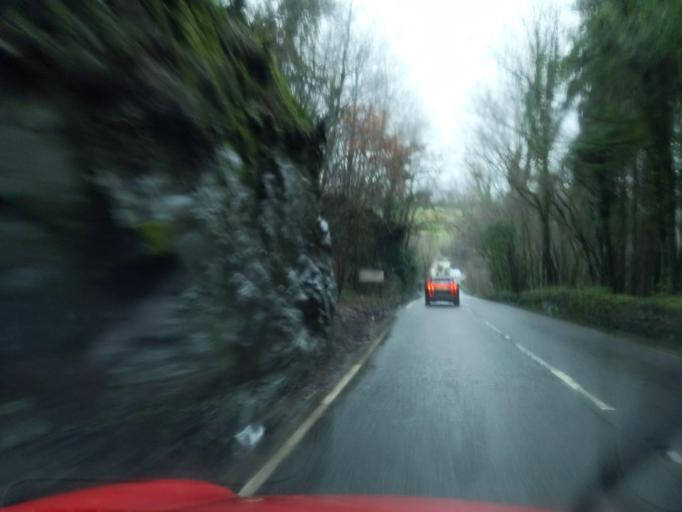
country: GB
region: England
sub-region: Cornwall
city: South Hill
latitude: 50.5672
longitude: -4.3349
